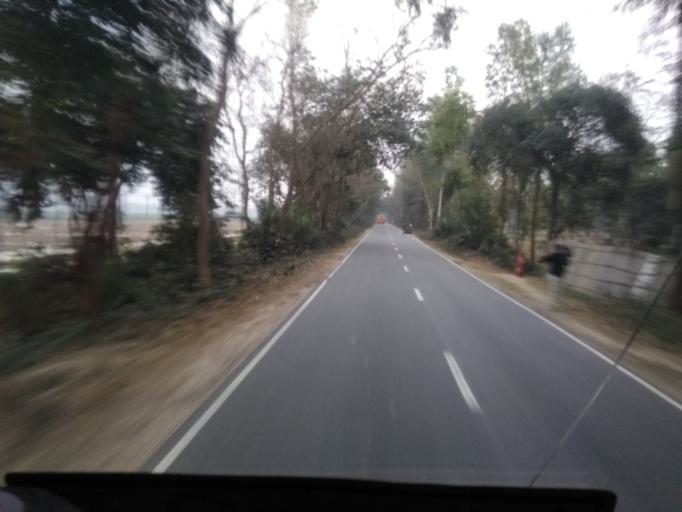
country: BD
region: Rajshahi
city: Bogra
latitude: 24.6943
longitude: 89.2995
